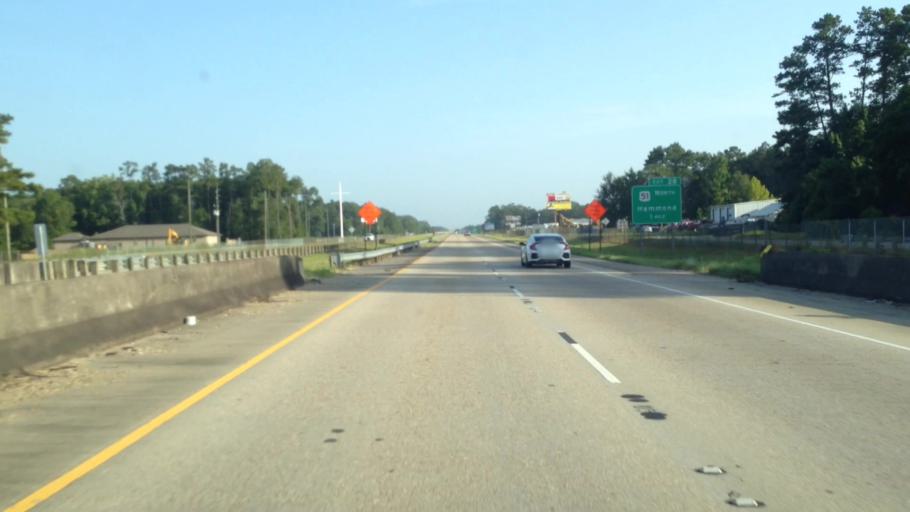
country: US
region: Louisiana
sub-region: Tangipahoa Parish
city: Ponchatoula
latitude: 30.4552
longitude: -90.4723
